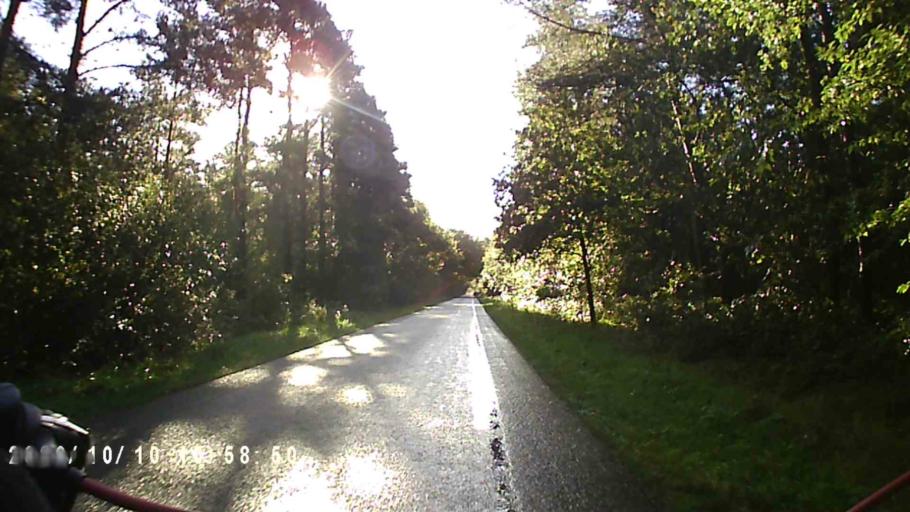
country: NL
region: Friesland
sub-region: Gemeente Achtkarspelen
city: Surhuisterveen
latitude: 53.1439
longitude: 6.2077
